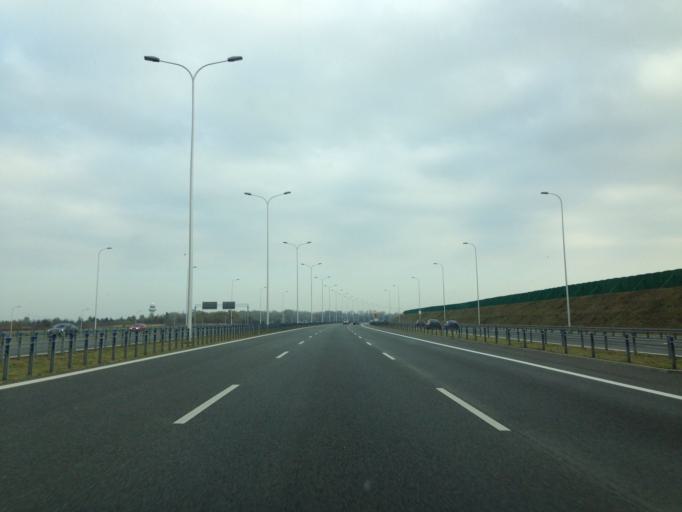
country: PL
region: Masovian Voivodeship
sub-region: Powiat pruszkowski
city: Rybie
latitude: 52.1649
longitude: 20.9396
